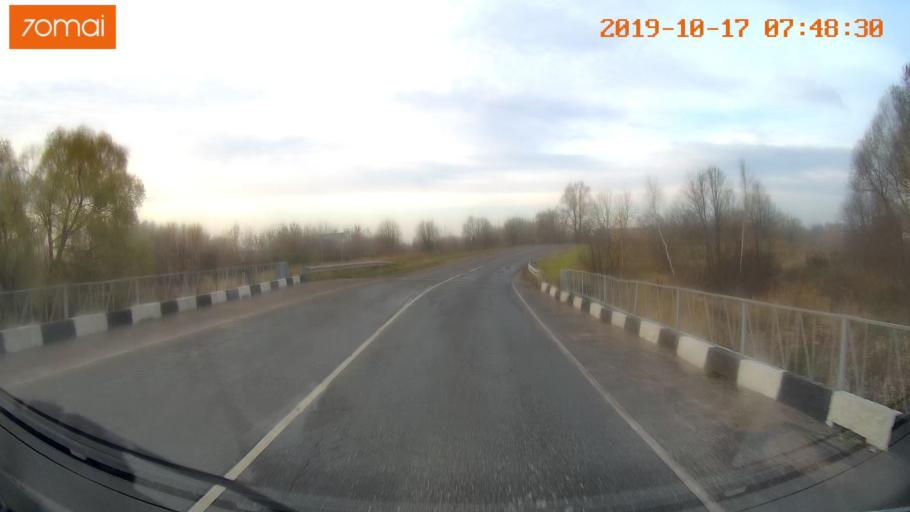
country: RU
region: Vladimir
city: Yur'yev-Pol'skiy
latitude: 56.4794
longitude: 39.6751
